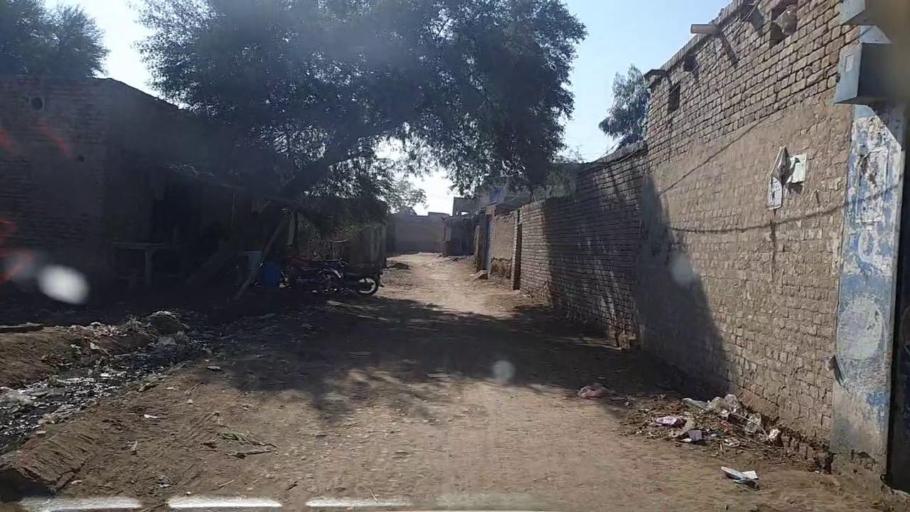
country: PK
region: Sindh
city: Khairpur
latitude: 27.9571
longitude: 69.6862
